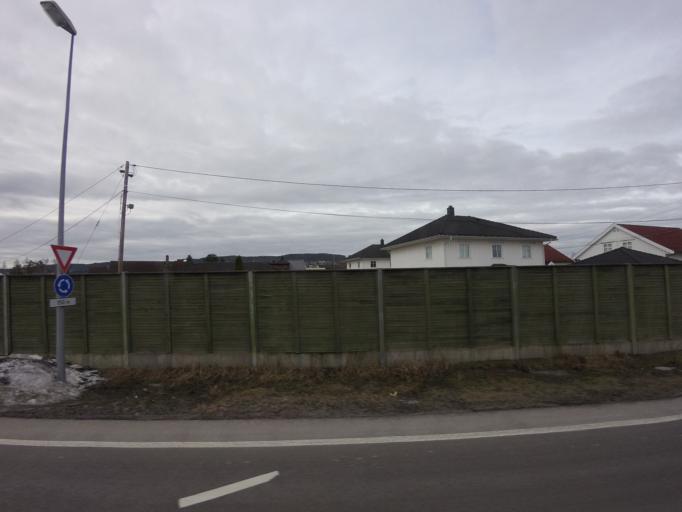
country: NO
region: Akershus
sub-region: Skedsmo
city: Lillestrom
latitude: 59.9543
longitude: 11.0758
